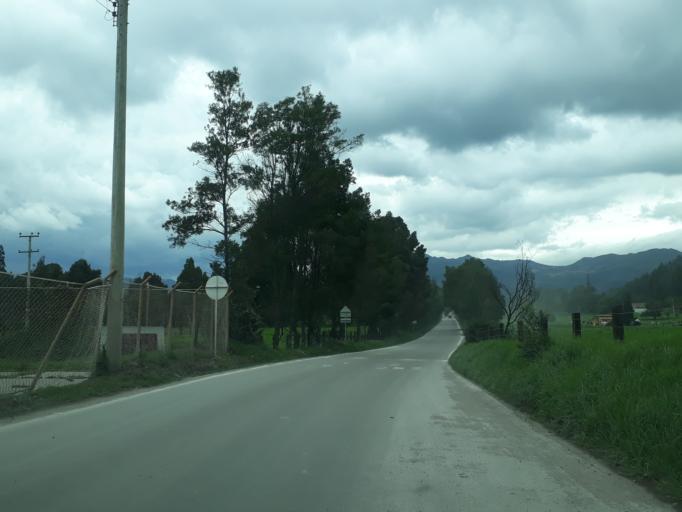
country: CO
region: Cundinamarca
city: Lenguazaque
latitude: 5.3282
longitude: -73.7368
